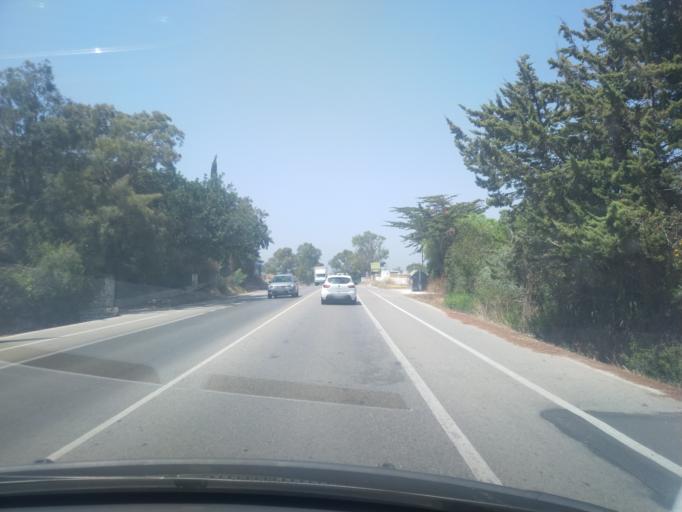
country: ES
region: Andalusia
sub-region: Provincia de Cadiz
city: Chiclana de la Frontera
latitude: 36.3918
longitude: -6.1433
